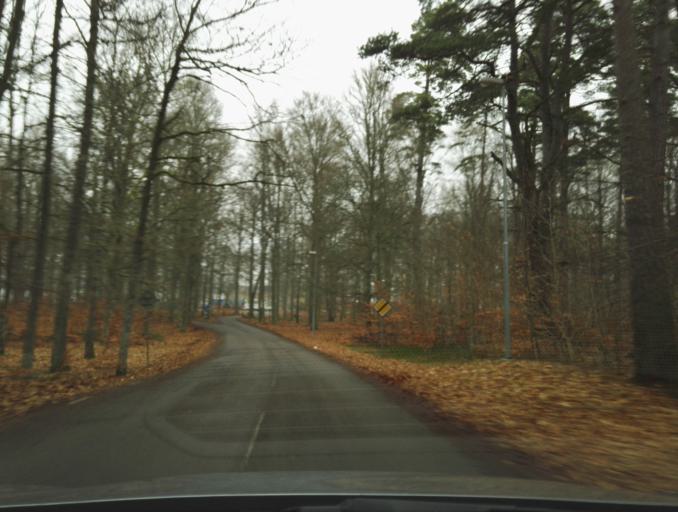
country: SE
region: Kronoberg
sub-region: Vaxjo Kommun
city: Vaexjoe
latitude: 56.9391
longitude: 14.7971
